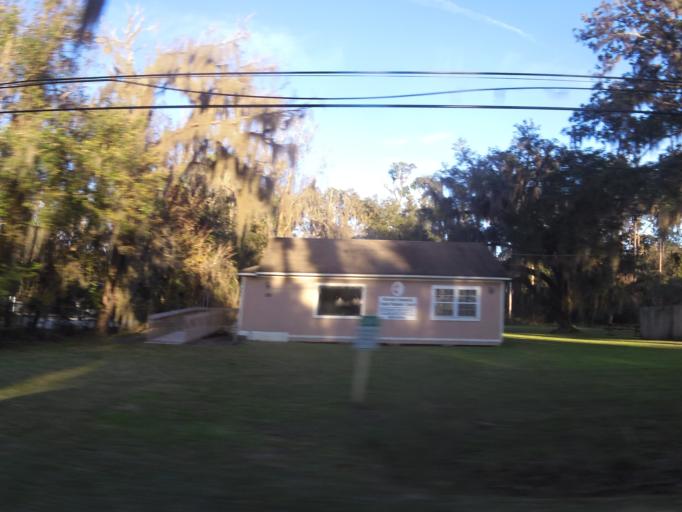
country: US
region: Florida
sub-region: Putnam County
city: East Palatka
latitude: 29.8213
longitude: -81.5518
